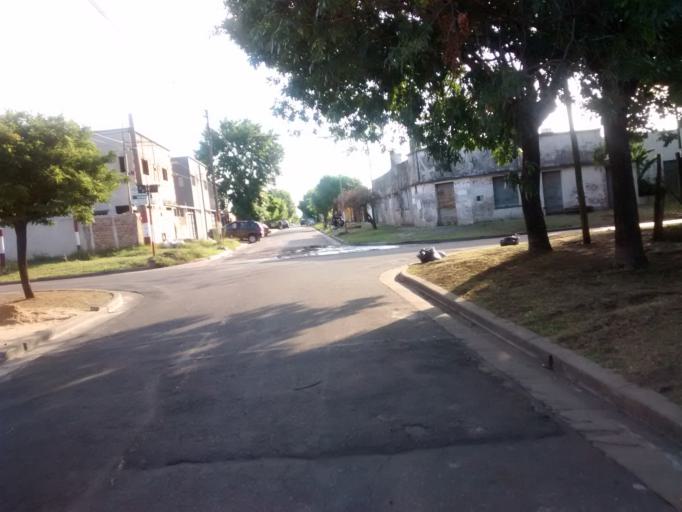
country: AR
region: Buenos Aires
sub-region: Partido de La Plata
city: La Plata
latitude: -34.9411
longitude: -57.9301
